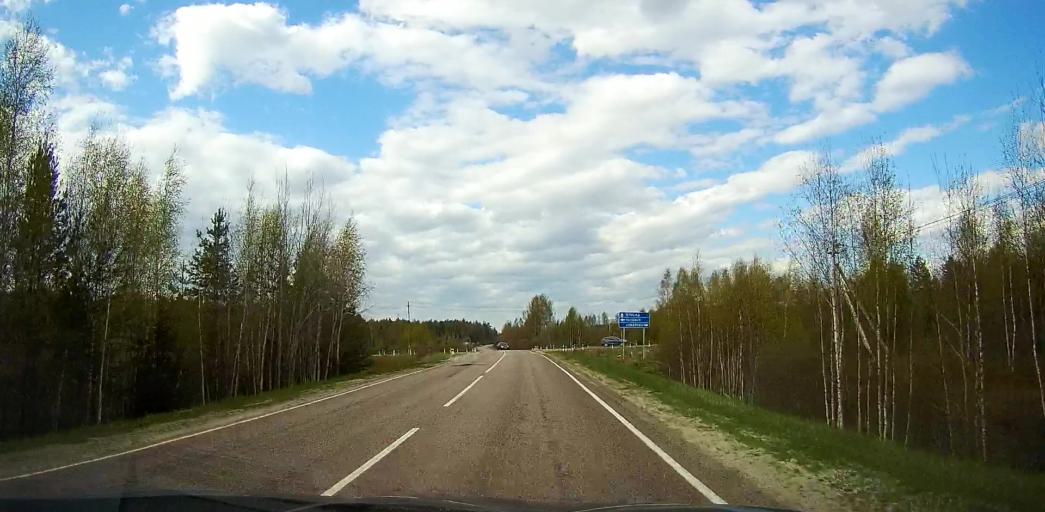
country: RU
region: Moskovskaya
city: Rakhmanovo
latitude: 55.6768
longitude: 38.6448
